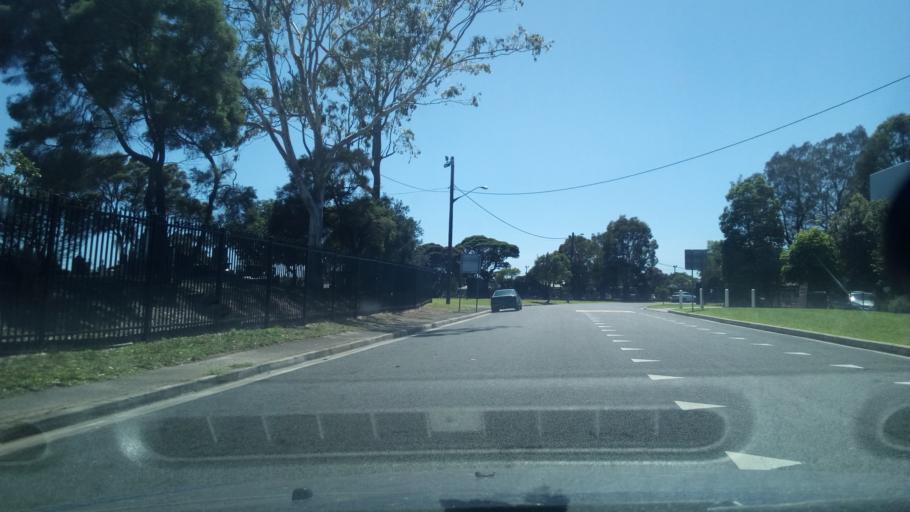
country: AU
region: New South Wales
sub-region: Wollongong
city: Coniston
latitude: -34.4380
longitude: 150.8889
